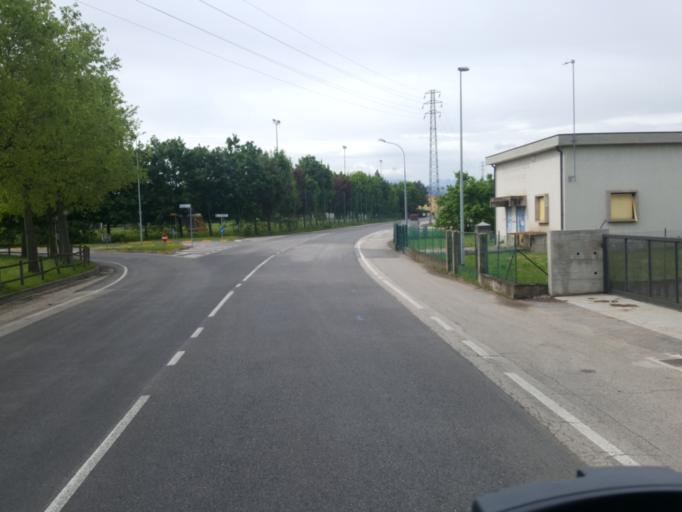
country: IT
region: Veneto
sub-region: Provincia di Vicenza
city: Montecchio Maggiore-Alte Ceccato
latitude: 45.4891
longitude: 11.4111
